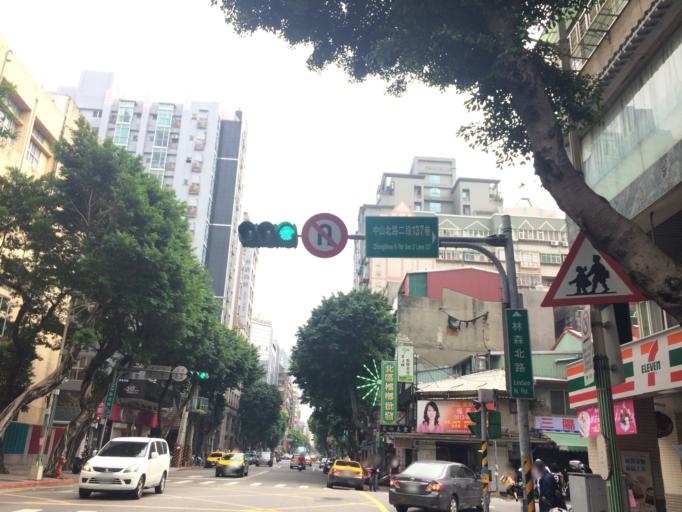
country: TW
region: Taipei
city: Taipei
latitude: 25.0620
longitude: 121.5257
